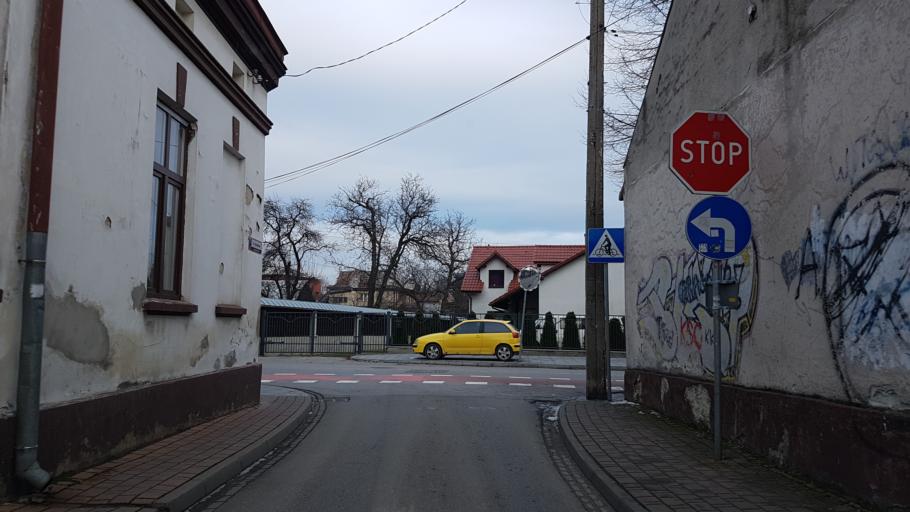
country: PL
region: Lesser Poland Voivodeship
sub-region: Powiat nowosadecki
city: Stary Sacz
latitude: 49.5601
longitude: 20.6353
